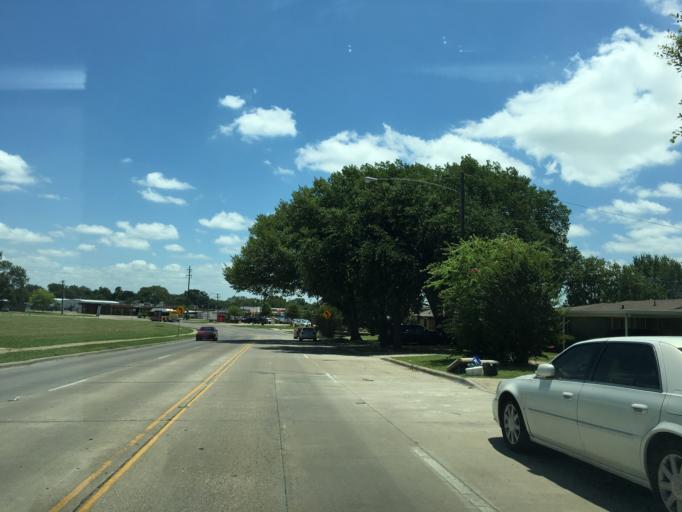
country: US
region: Texas
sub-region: Dallas County
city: Garland
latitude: 32.8427
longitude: -96.6681
